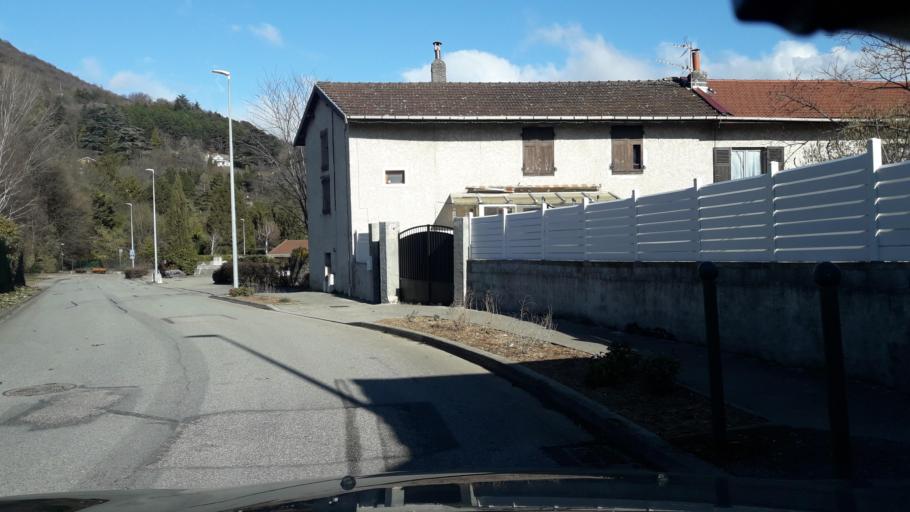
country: FR
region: Rhone-Alpes
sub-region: Departement de l'Isere
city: Seyssinet-Pariset
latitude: 45.1690
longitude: 5.6840
